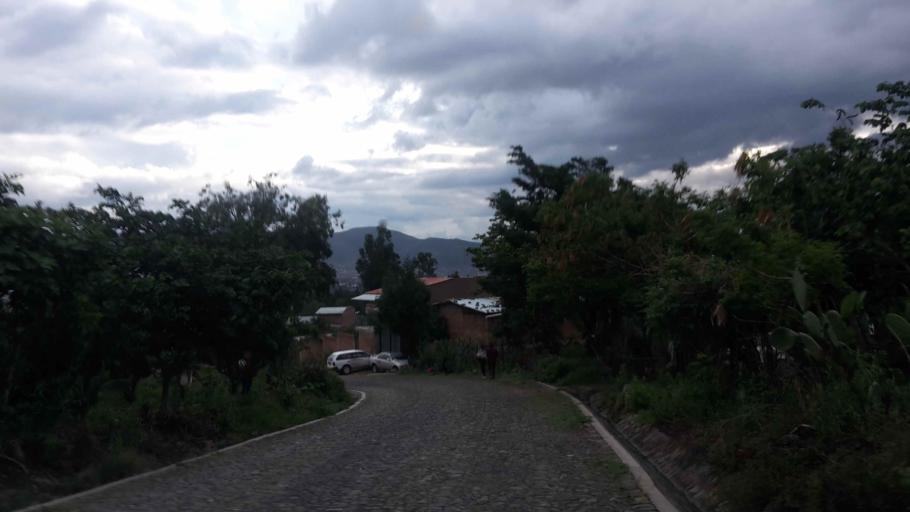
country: BO
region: Cochabamba
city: Cochabamba
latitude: -17.3739
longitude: -66.0554
